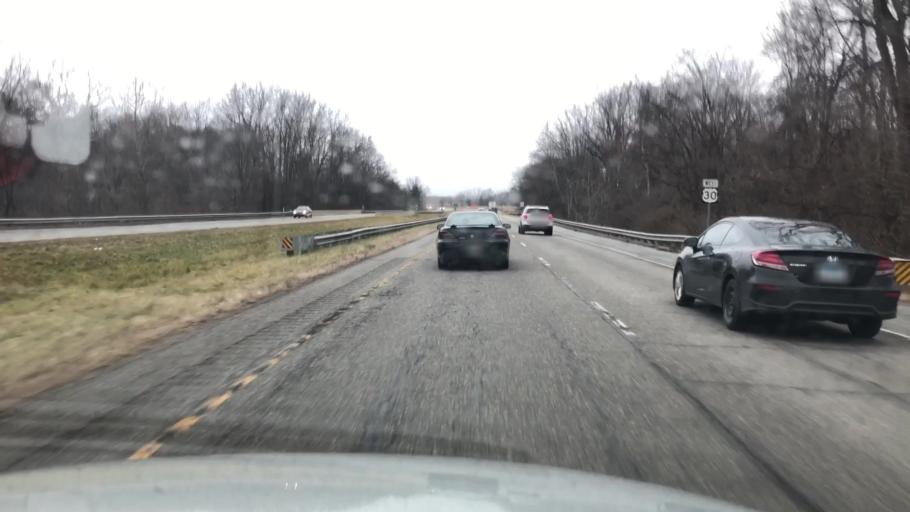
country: US
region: Indiana
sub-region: Marshall County
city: Plymouth
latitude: 41.3540
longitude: -86.2797
